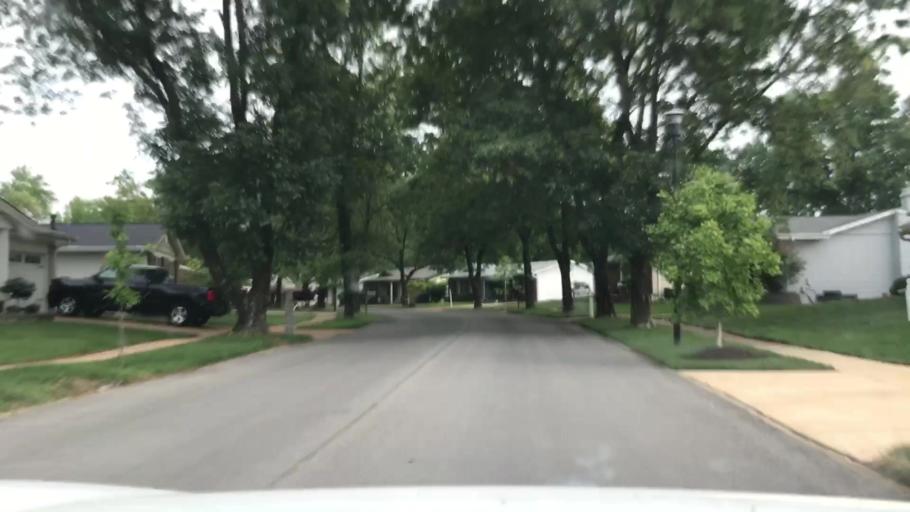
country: US
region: Missouri
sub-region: Saint Louis County
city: Ballwin
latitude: 38.5816
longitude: -90.5629
